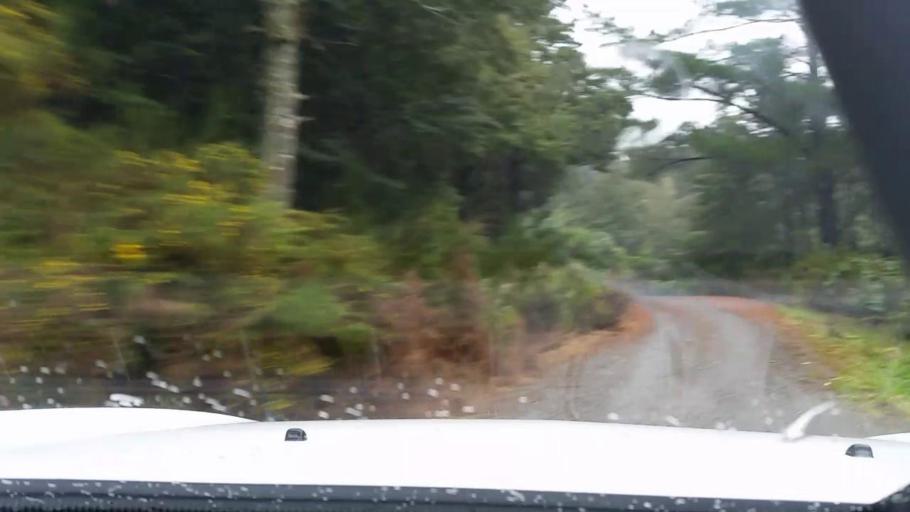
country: NZ
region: Wellington
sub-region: Masterton District
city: Masterton
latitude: -41.1584
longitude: 175.8027
